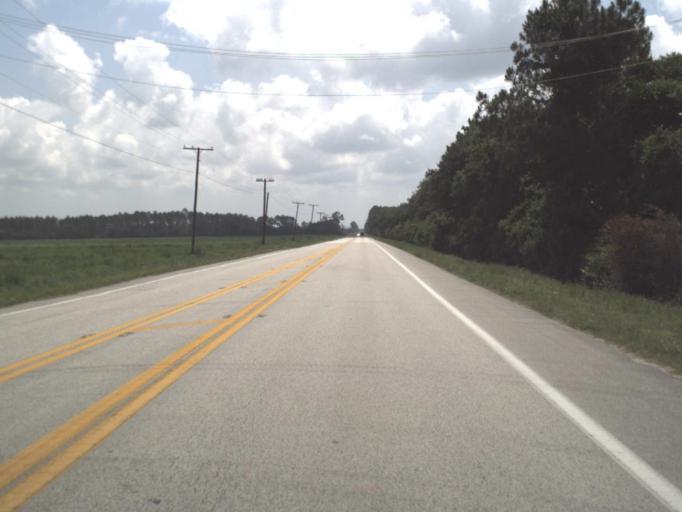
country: US
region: Florida
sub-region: Putnam County
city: East Palatka
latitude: 29.7255
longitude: -81.4622
